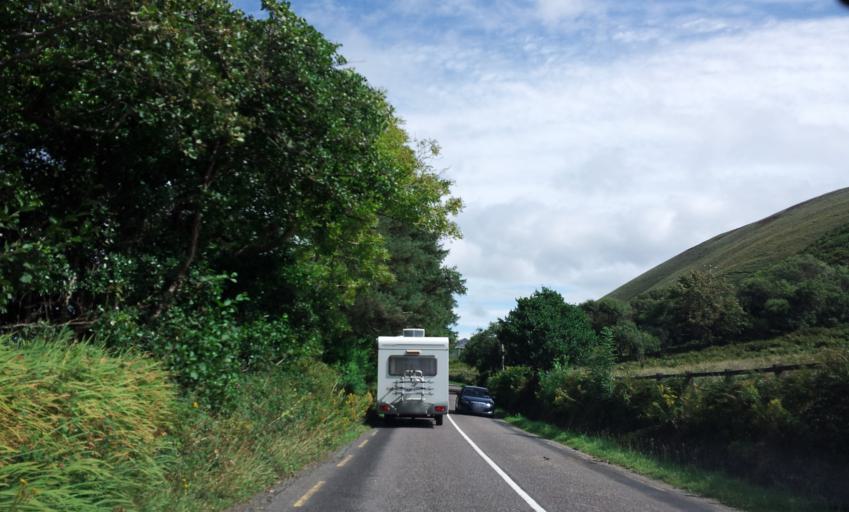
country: IE
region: Munster
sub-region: Ciarrai
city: Killorglin
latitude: 52.0547
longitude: -9.9687
